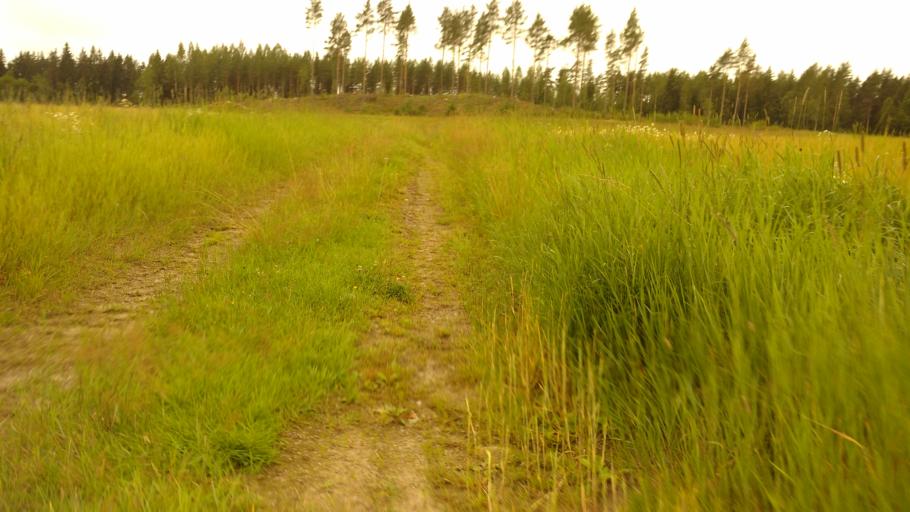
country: FI
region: Varsinais-Suomi
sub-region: Salo
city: Pertteli
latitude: 60.3998
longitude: 23.2295
